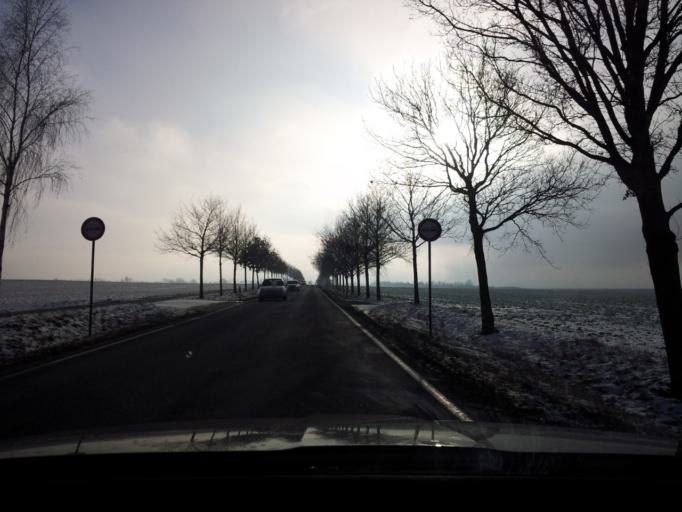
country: DE
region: Mecklenburg-Vorpommern
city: Blowatz
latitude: 53.9568
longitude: 11.4879
